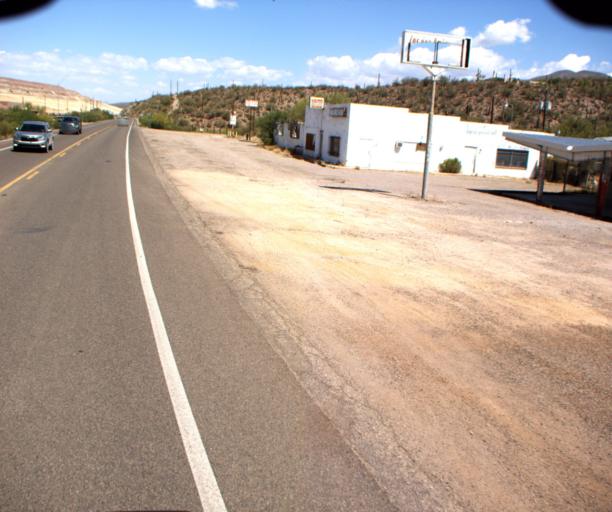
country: US
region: Arizona
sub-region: Pinal County
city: Kearny
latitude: 32.9886
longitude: -110.7774
